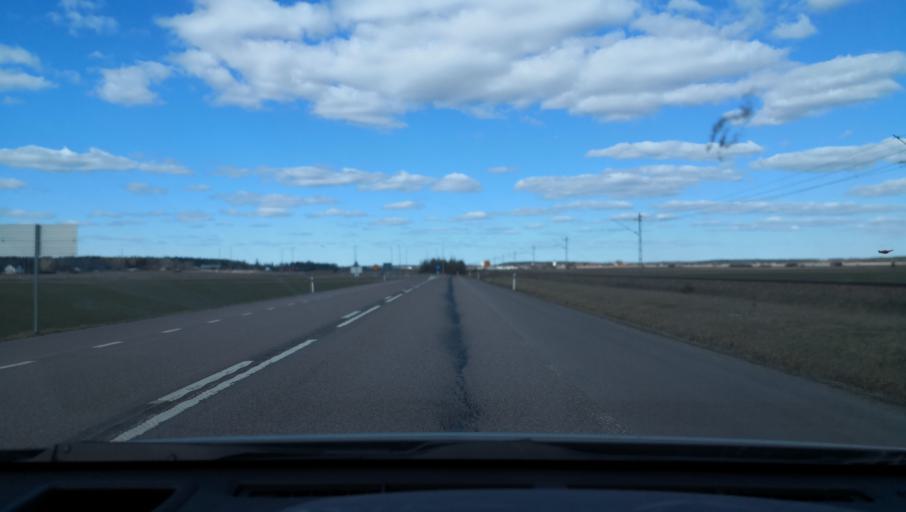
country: SE
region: Vaestmanland
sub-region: Sala Kommun
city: Sala
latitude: 59.8849
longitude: 16.6245
